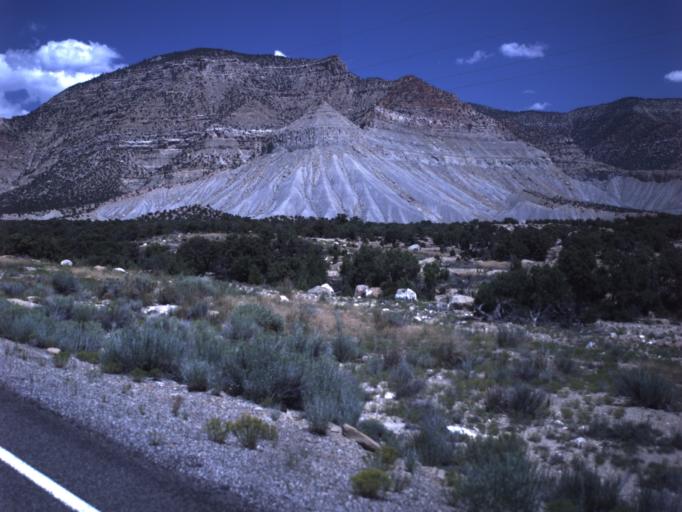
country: US
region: Utah
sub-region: Emery County
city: Orangeville
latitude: 39.2876
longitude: -111.1080
